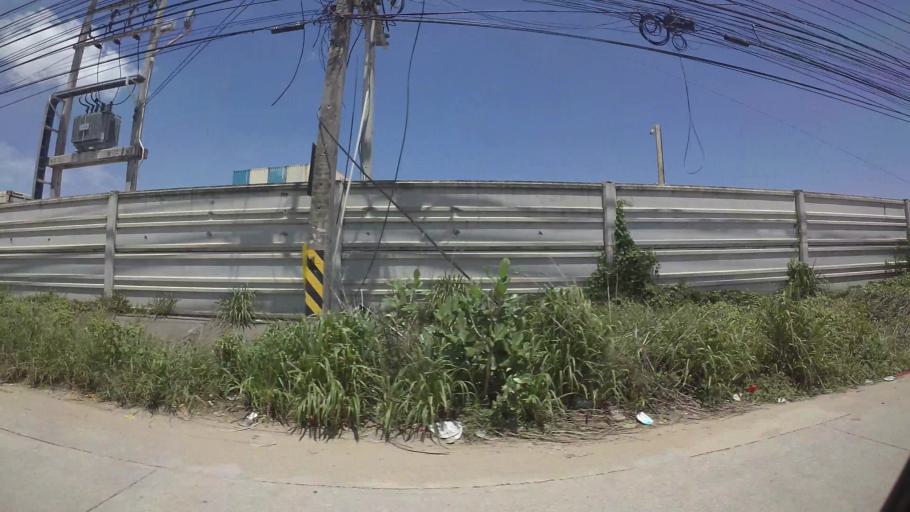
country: TH
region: Chon Buri
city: Si Racha
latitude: 13.1193
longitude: 100.9564
